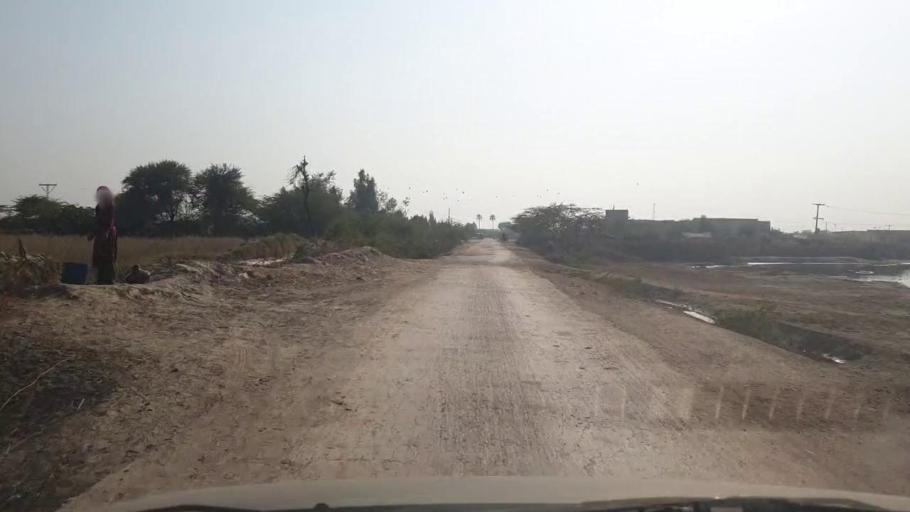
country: PK
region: Sindh
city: Digri
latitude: 25.2512
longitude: 69.1826
